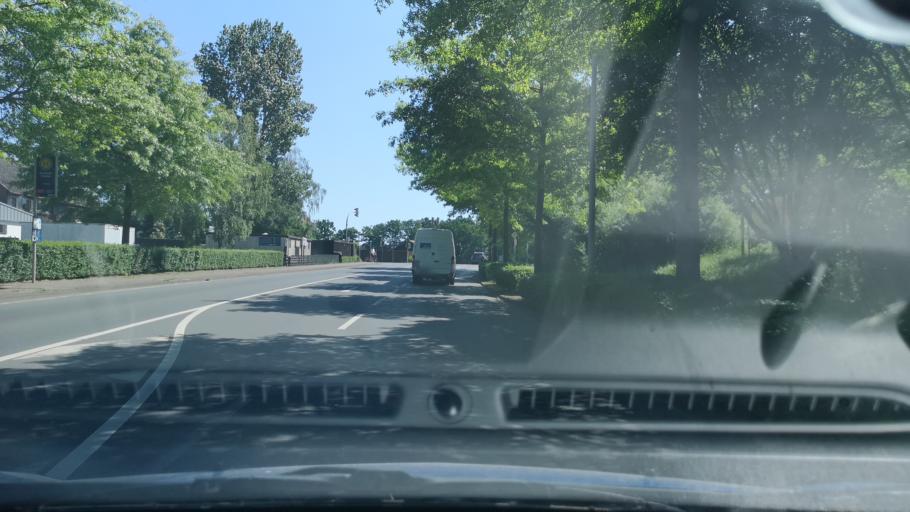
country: DE
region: Lower Saxony
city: Garbsen-Mitte
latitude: 52.4405
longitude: 9.6201
